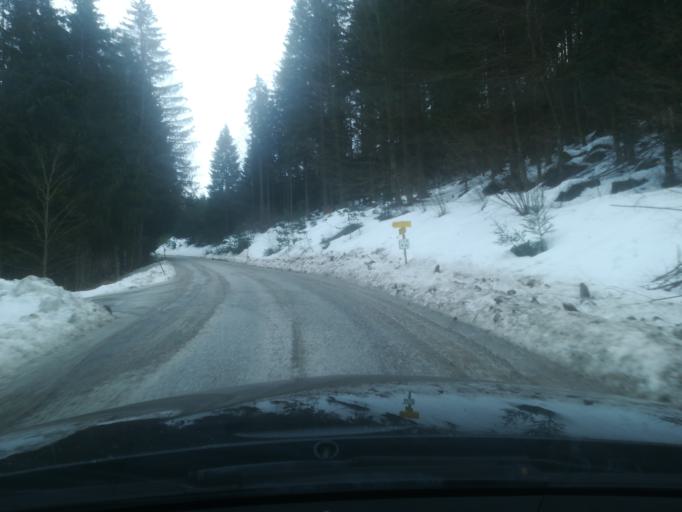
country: AT
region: Upper Austria
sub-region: Politischer Bezirk Perg
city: Perg
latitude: 48.4181
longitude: 14.6497
